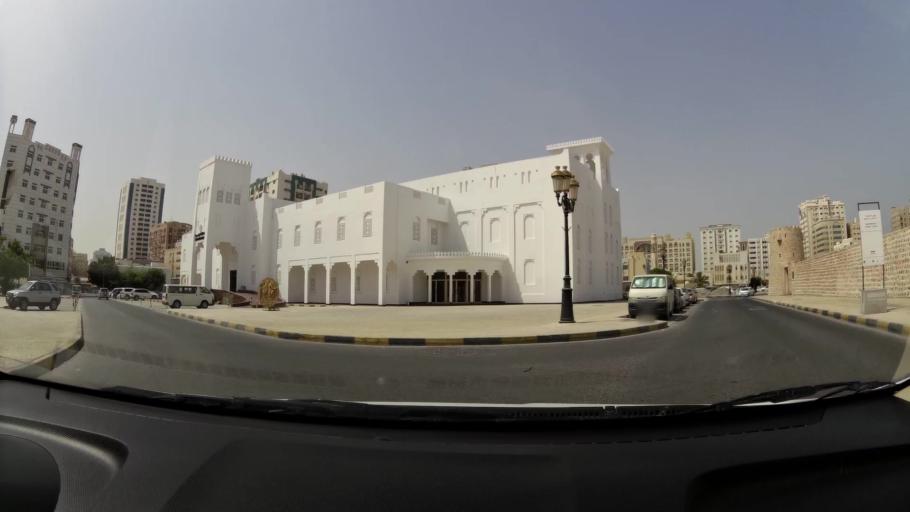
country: AE
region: Ash Shariqah
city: Sharjah
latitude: 25.3568
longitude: 55.3850
